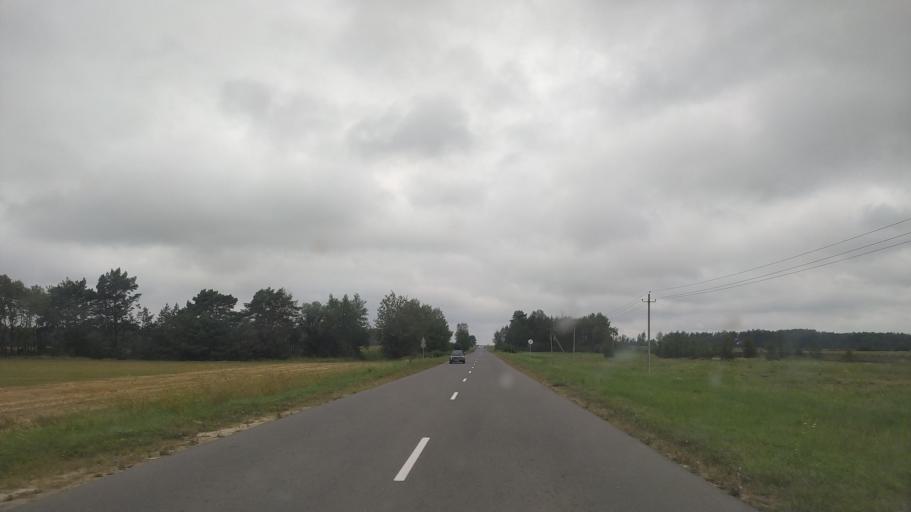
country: BY
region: Brest
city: Byaroza
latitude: 52.5595
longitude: 24.9114
